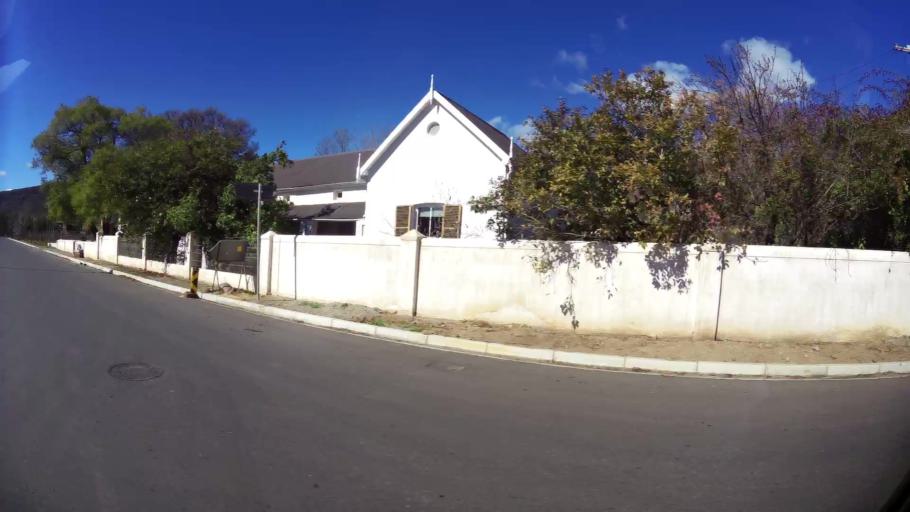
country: ZA
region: Western Cape
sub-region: Cape Winelands District Municipality
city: Ashton
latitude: -33.7878
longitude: 20.1282
